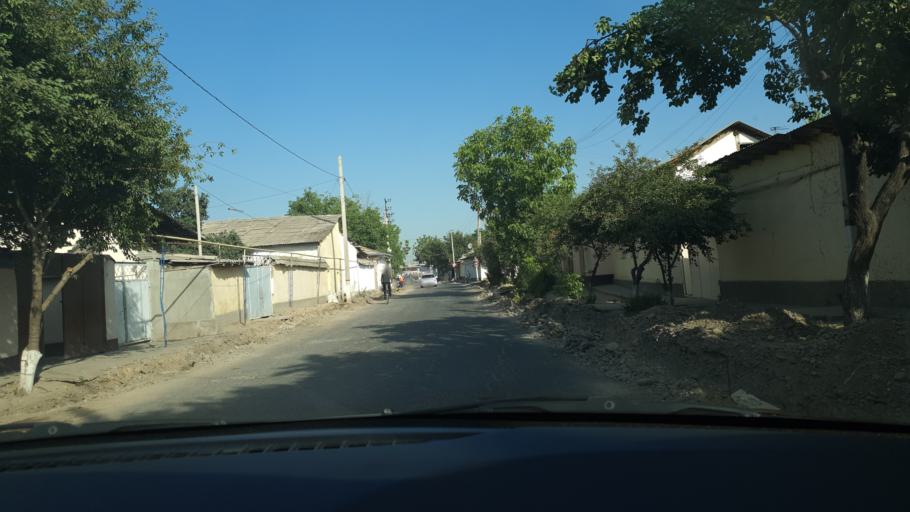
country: UZ
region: Toshkent
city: Urtaowul
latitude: 41.2001
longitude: 69.1584
